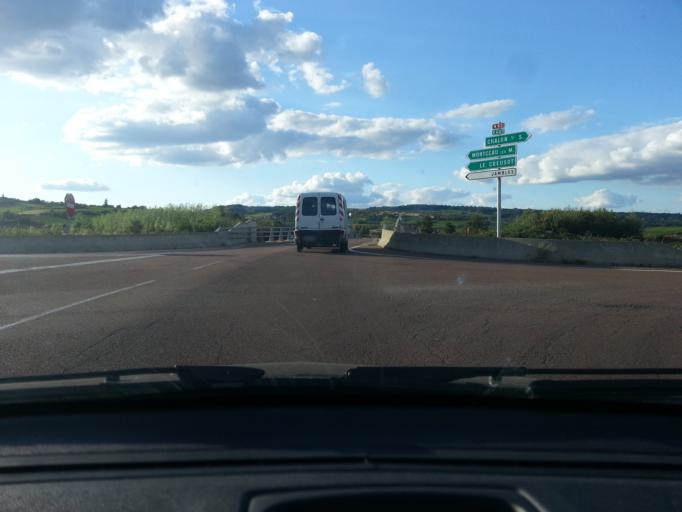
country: FR
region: Bourgogne
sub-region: Departement de Saone-et-Loire
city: Givry
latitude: 46.7569
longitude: 4.7192
